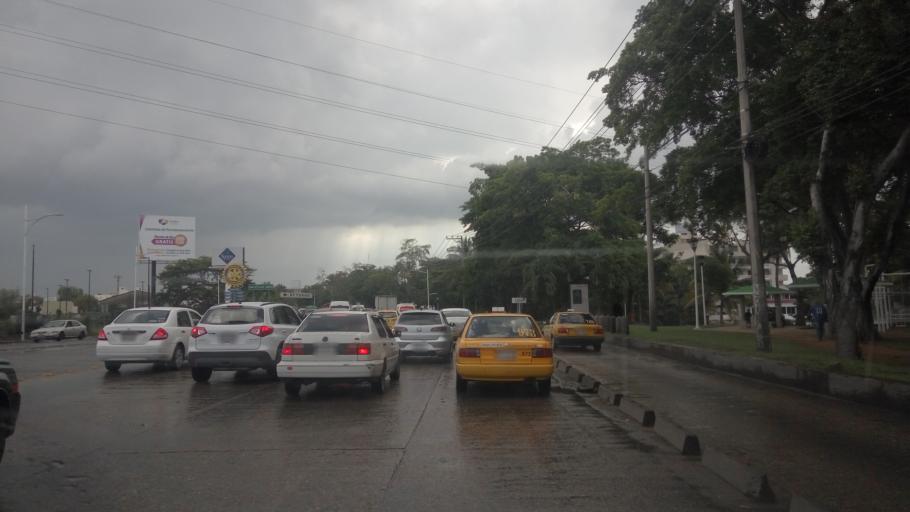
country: MX
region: Tabasco
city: Villahermosa
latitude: 18.0056
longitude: -92.9248
